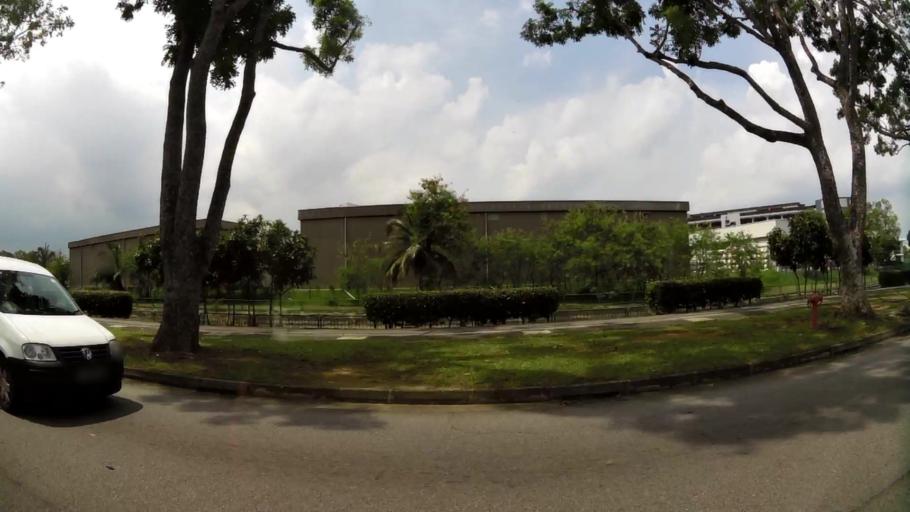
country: MY
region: Johor
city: Kampung Pasir Gudang Baru
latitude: 1.3785
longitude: 103.9785
